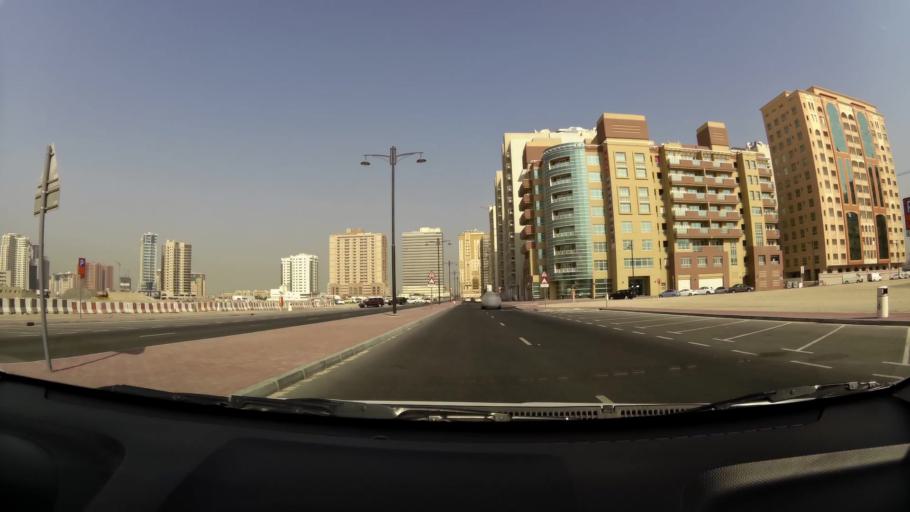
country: AE
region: Ash Shariqah
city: Sharjah
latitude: 25.2943
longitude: 55.3673
